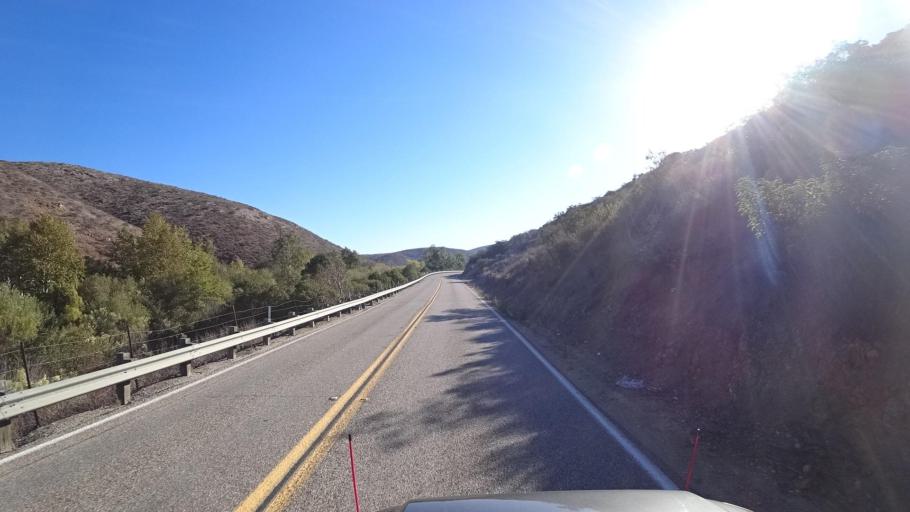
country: US
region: California
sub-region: San Diego County
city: Jamul
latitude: 32.6403
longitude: -116.8801
